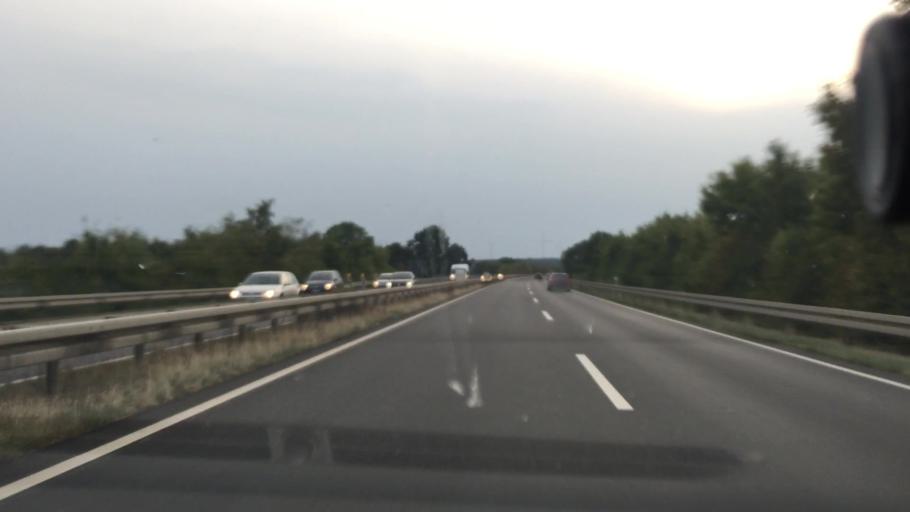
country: DE
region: Lower Saxony
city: Marklohe
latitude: 52.6536
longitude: 9.1716
